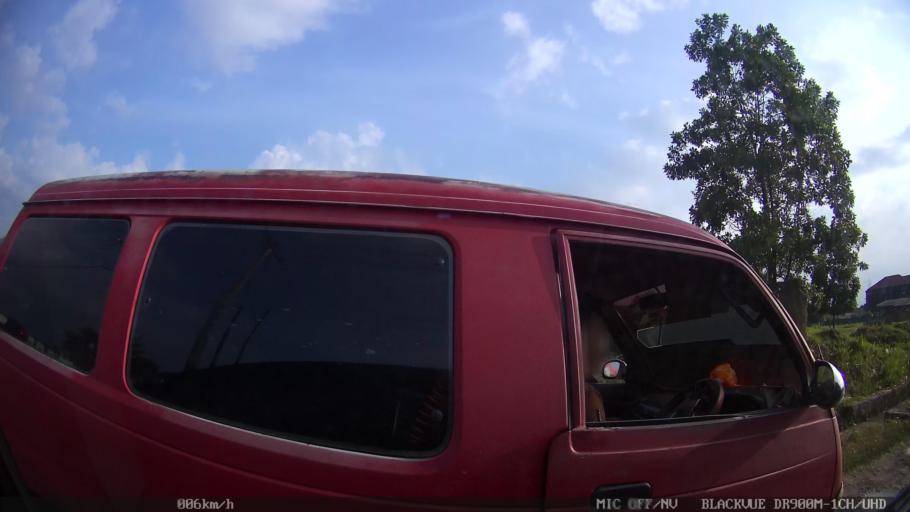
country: ID
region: Lampung
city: Kedaton
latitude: -5.3909
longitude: 105.3095
